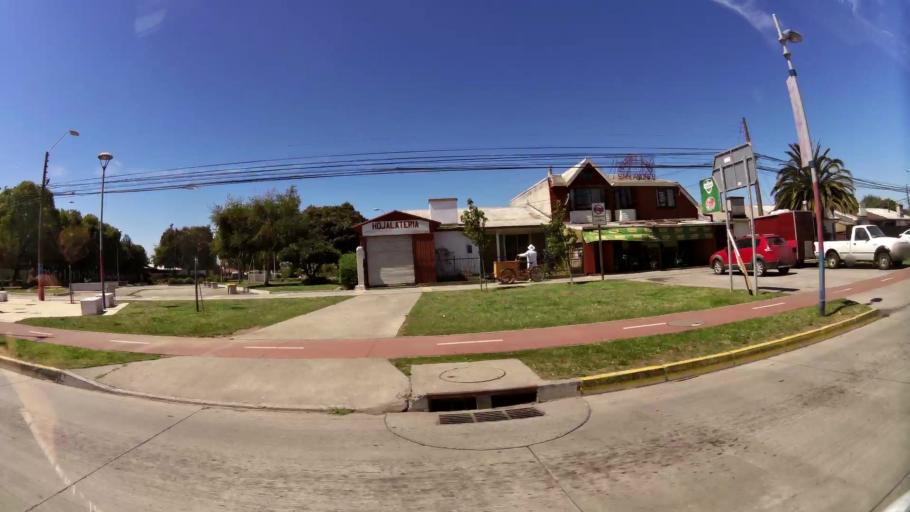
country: CL
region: Biobio
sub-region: Provincia de Concepcion
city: Talcahuano
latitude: -36.7483
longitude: -73.0941
